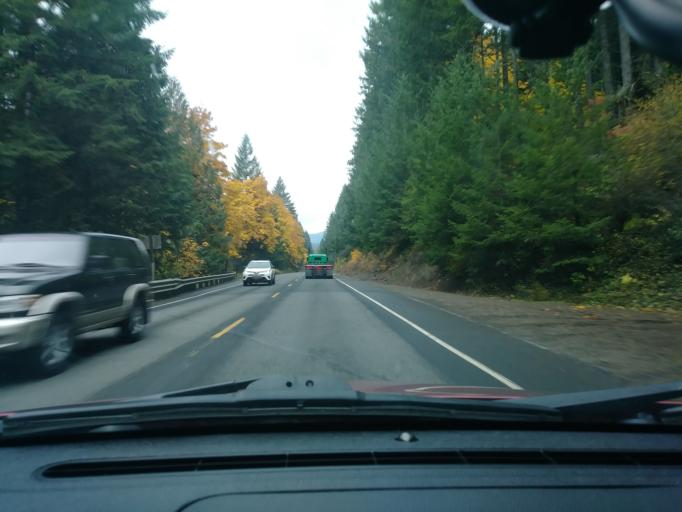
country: US
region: Oregon
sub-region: Washington County
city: Banks
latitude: 45.6514
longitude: -123.2807
